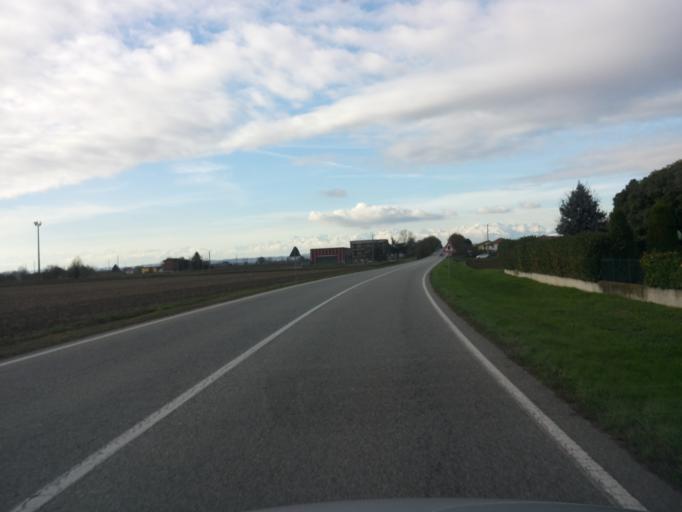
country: IT
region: Piedmont
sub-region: Provincia di Vercelli
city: Tronzano Vercellese
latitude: 45.3381
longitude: 8.1725
